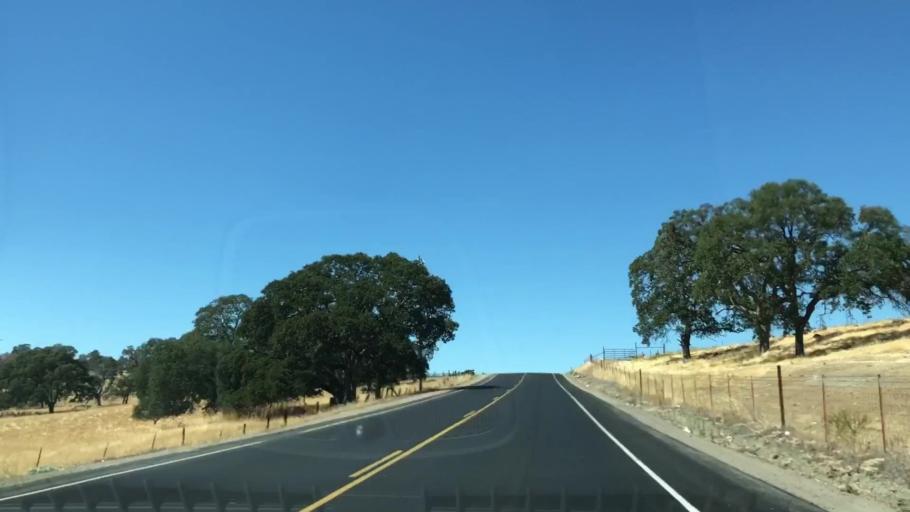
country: US
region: California
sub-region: Tuolumne County
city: Jamestown
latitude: 37.8808
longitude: -120.4727
